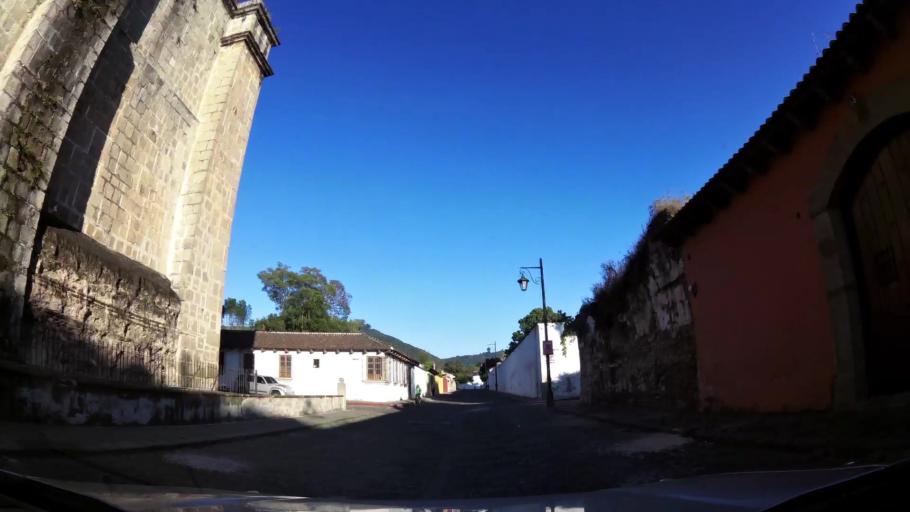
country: GT
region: Sacatepequez
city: Antigua Guatemala
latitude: 14.5593
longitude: -90.7313
